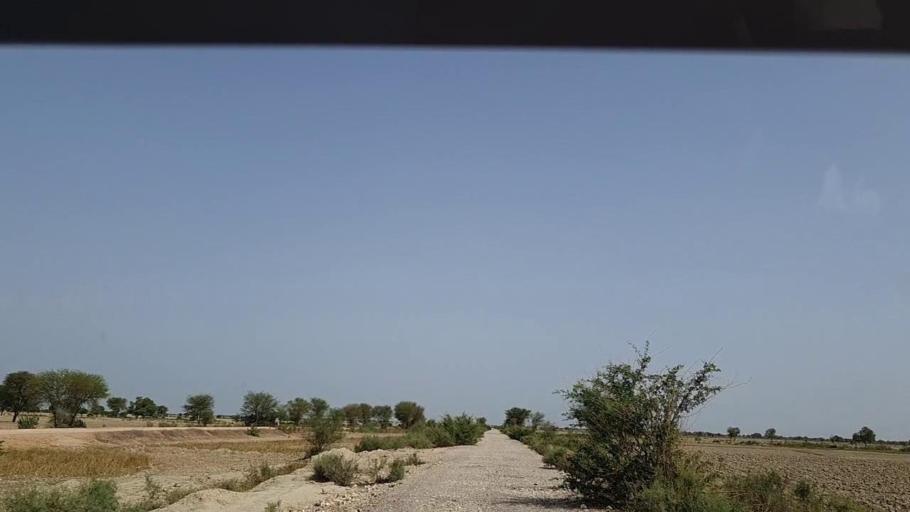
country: PK
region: Sindh
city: Johi
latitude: 26.7513
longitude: 67.6705
